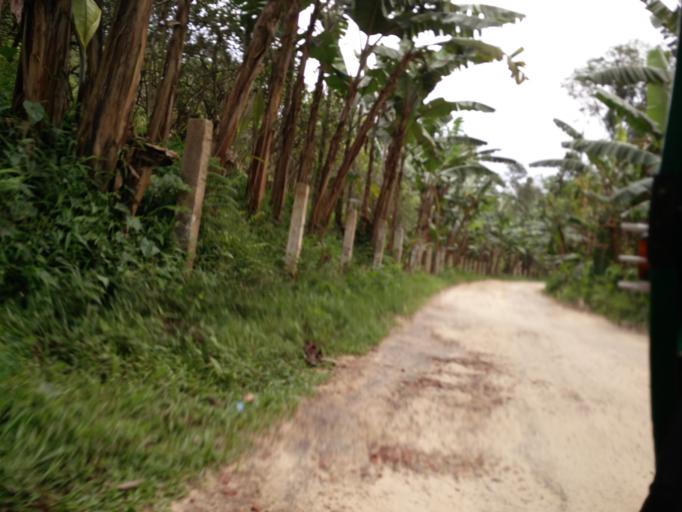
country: IN
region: Tripura
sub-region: Dhalai
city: Kamalpur
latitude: 24.3023
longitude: 91.7812
